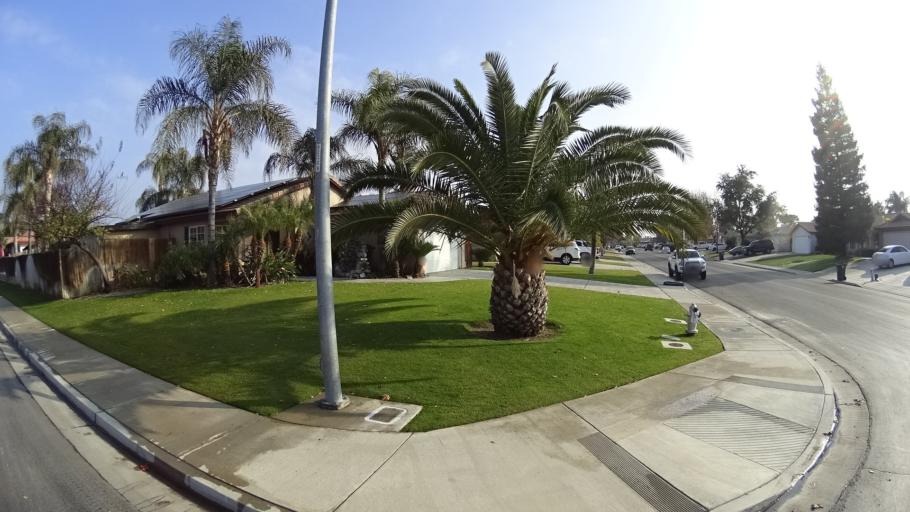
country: US
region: California
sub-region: Kern County
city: Greenfield
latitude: 35.2997
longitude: -119.0676
